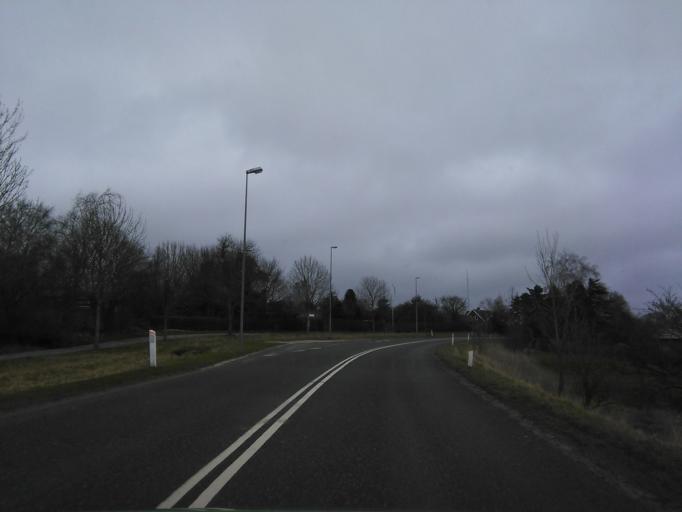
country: DK
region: Central Jutland
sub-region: Arhus Kommune
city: Beder
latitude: 56.0893
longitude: 10.1910
